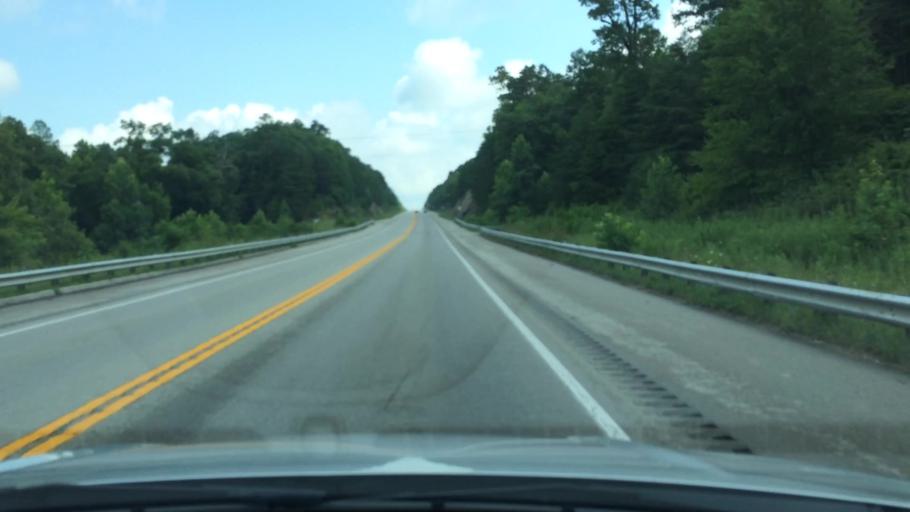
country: US
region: Kentucky
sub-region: McCreary County
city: Whitley City
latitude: 36.8234
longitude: -84.4851
